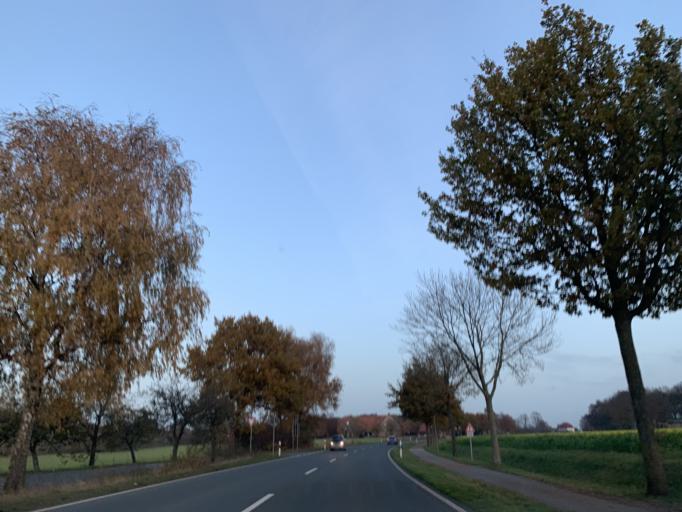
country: DE
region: North Rhine-Westphalia
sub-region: Regierungsbezirk Munster
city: Billerbeck
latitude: 51.9735
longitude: 7.3311
